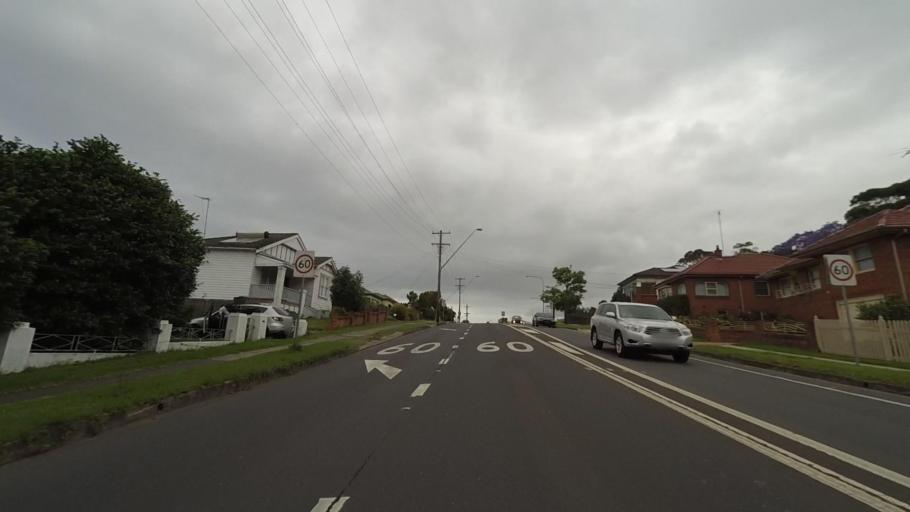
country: AU
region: New South Wales
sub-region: Wollongong
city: Bulli
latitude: -34.3212
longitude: 150.9138
